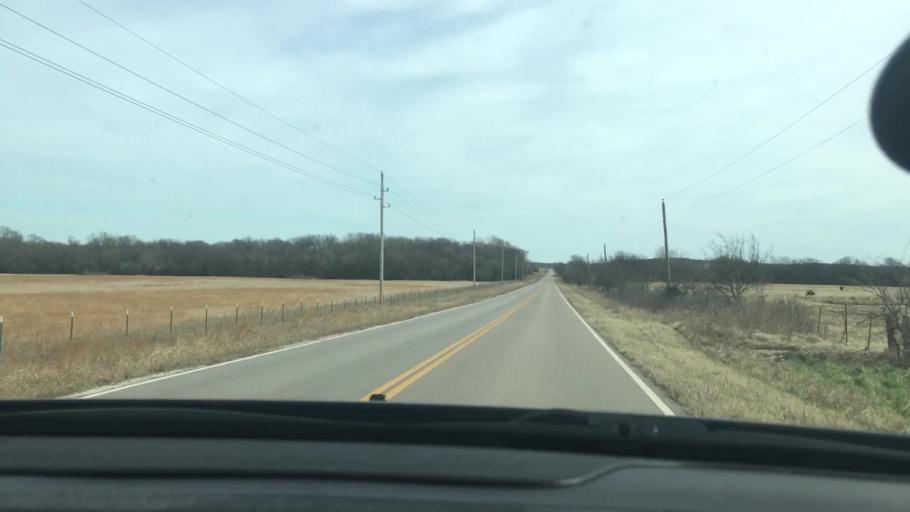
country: US
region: Oklahoma
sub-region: Murray County
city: Sulphur
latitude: 34.4027
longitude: -96.8685
